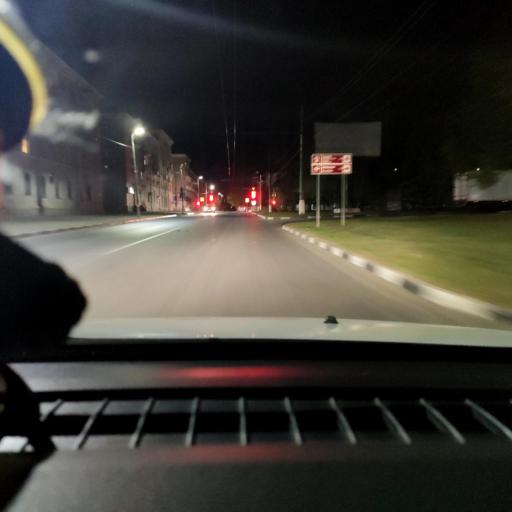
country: RU
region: Samara
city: Novokuybyshevsk
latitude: 53.1021
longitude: 49.9451
